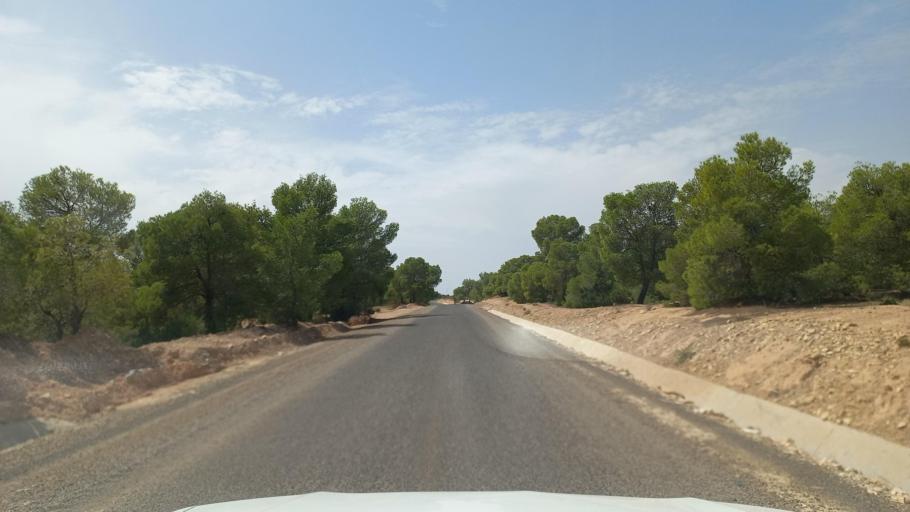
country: TN
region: Al Qasrayn
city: Kasserine
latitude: 35.3785
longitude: 8.9165
